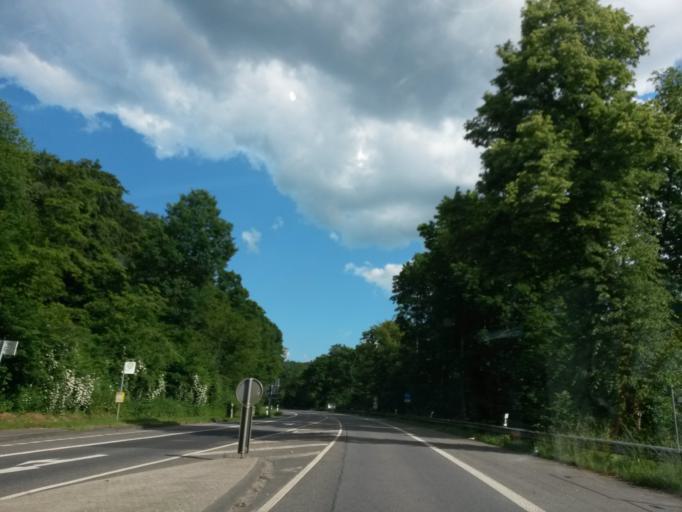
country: DE
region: North Rhine-Westphalia
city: Lohmar
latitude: 50.8453
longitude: 7.2271
